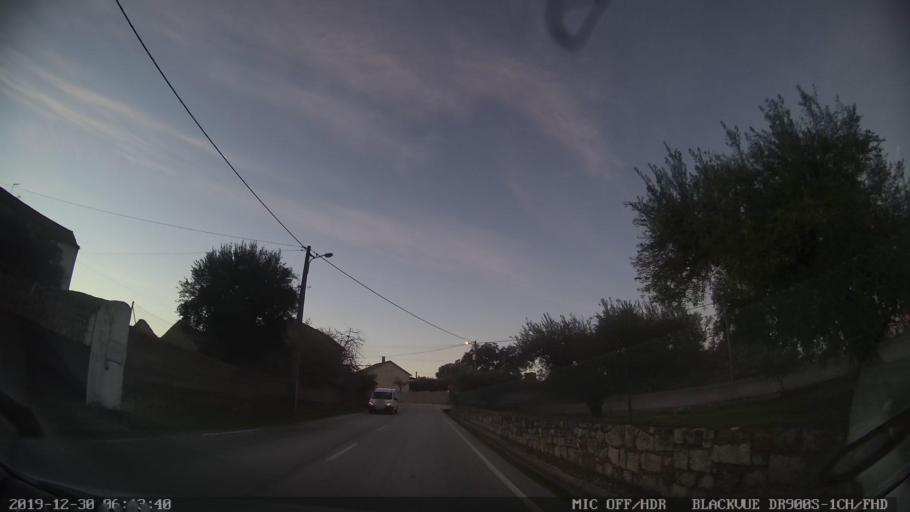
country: PT
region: Castelo Branco
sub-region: Penamacor
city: Penamacor
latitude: 40.1120
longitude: -7.2119
